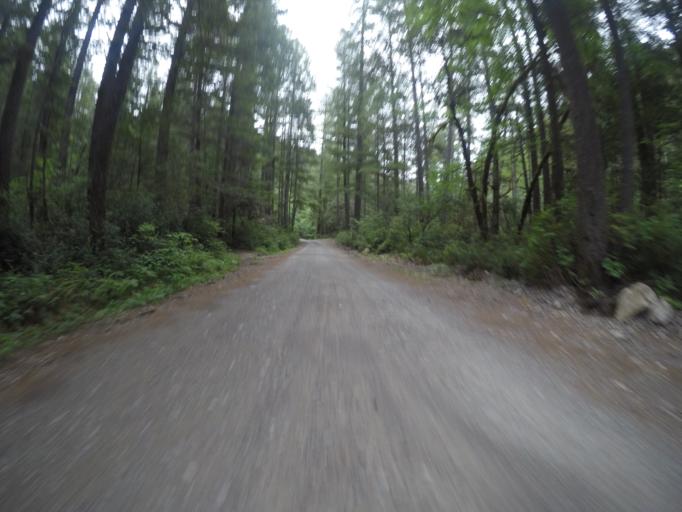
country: US
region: California
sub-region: Del Norte County
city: Bertsch-Oceanview
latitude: 41.7296
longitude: -123.8908
